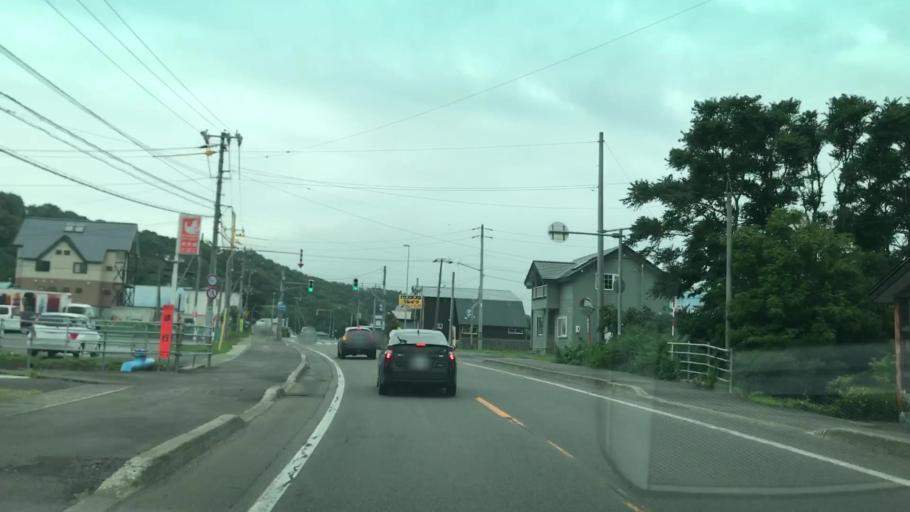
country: JP
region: Hokkaido
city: Iwanai
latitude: 42.7755
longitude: 140.3051
